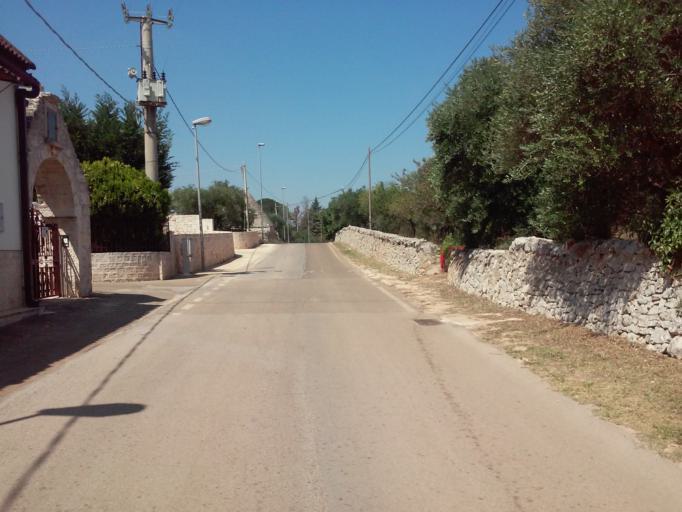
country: IT
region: Apulia
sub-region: Provincia di Bari
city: Alberobello
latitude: 40.7926
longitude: 17.2226
